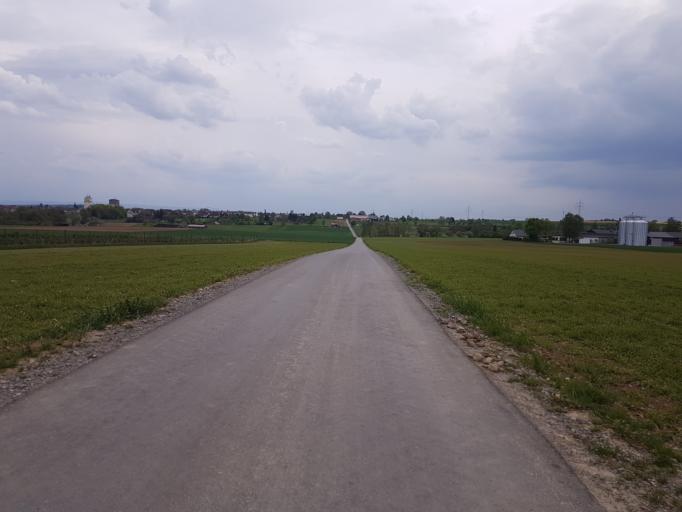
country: DE
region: Baden-Wuerttemberg
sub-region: Regierungsbezirk Stuttgart
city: Bondorf
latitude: 48.5314
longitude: 8.8220
